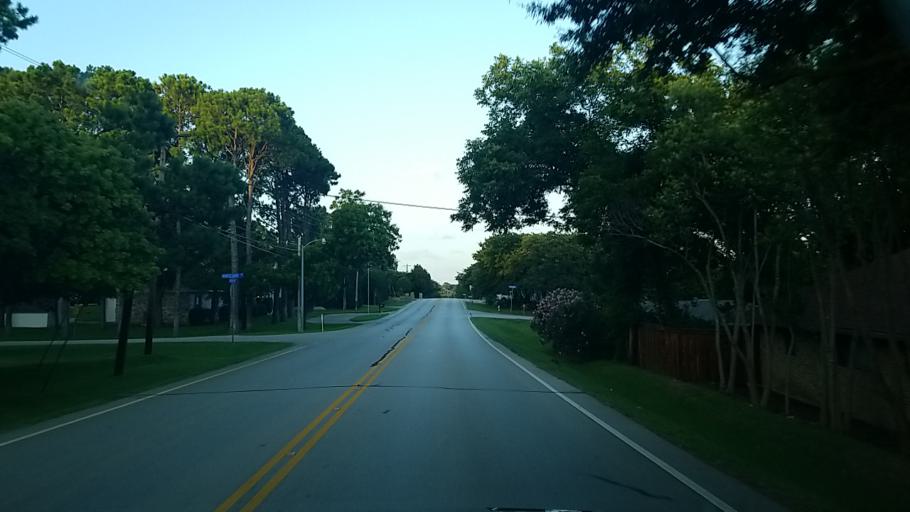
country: US
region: Texas
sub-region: Denton County
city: Highland Village
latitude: 33.0936
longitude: -97.0477
